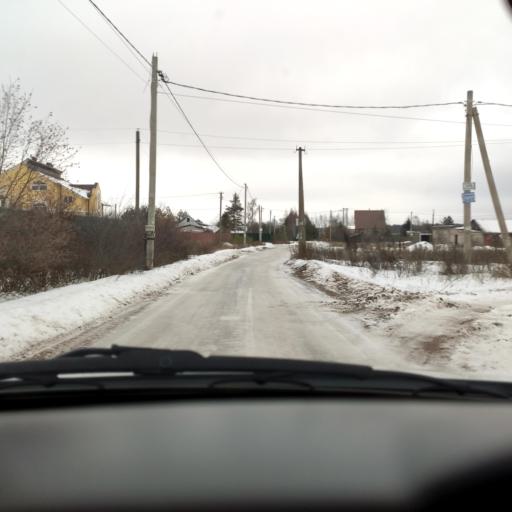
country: RU
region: Voronezj
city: Ramon'
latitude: 51.8857
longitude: 39.2627
